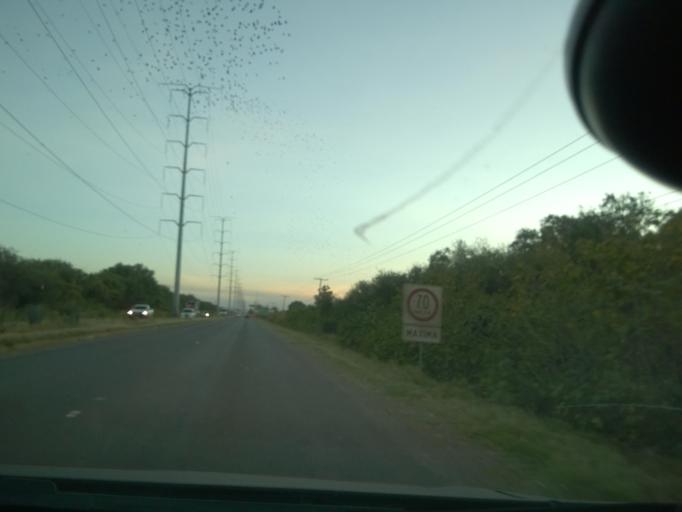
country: MX
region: Guanajuato
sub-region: Leon
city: Santa Ana
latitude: 21.0590
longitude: -101.6869
